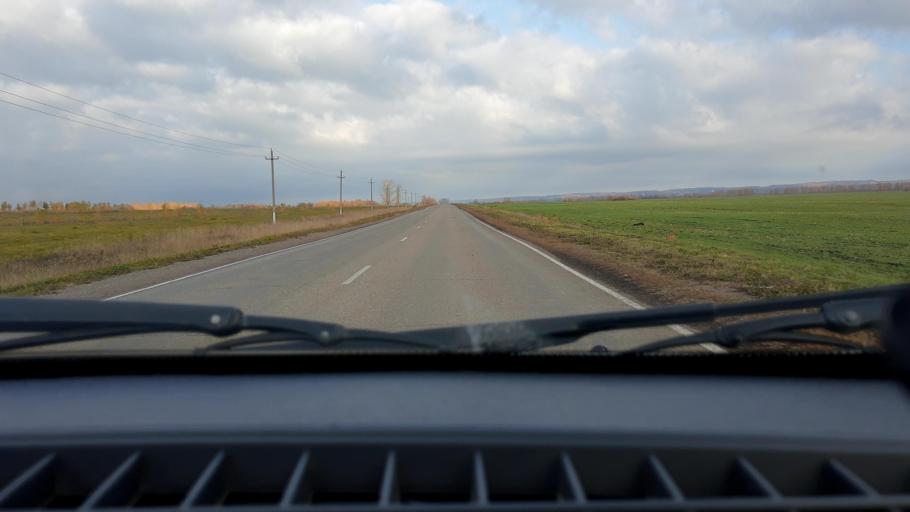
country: RU
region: Bashkortostan
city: Ulukulevo
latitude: 54.4037
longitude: 56.3766
